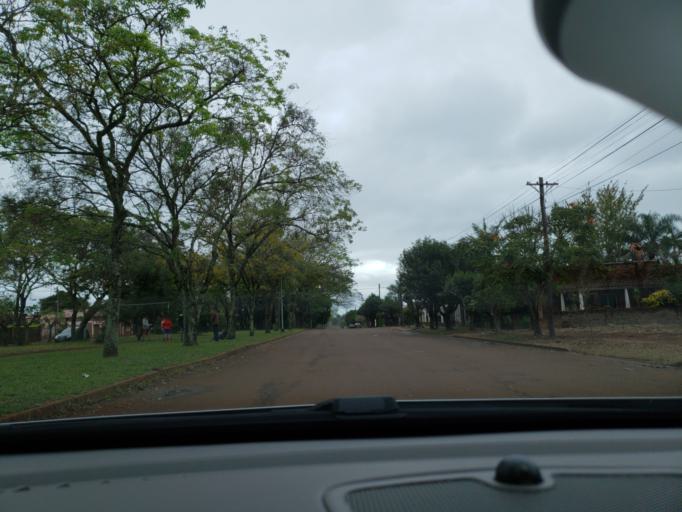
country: AR
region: Misiones
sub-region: Departamento de Apostoles
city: Apostoles
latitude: -27.9216
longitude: -55.7635
